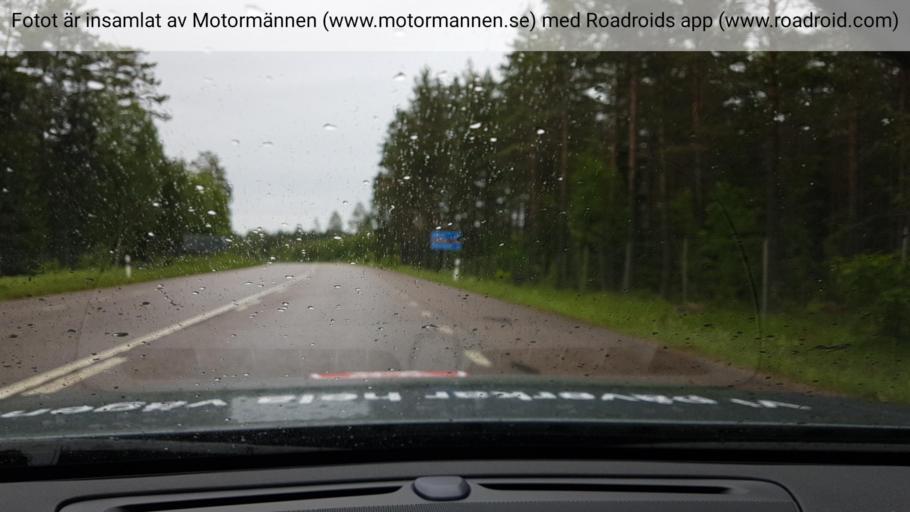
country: SE
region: Uppsala
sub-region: Alvkarleby Kommun
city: AElvkarleby
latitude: 60.5631
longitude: 17.4649
